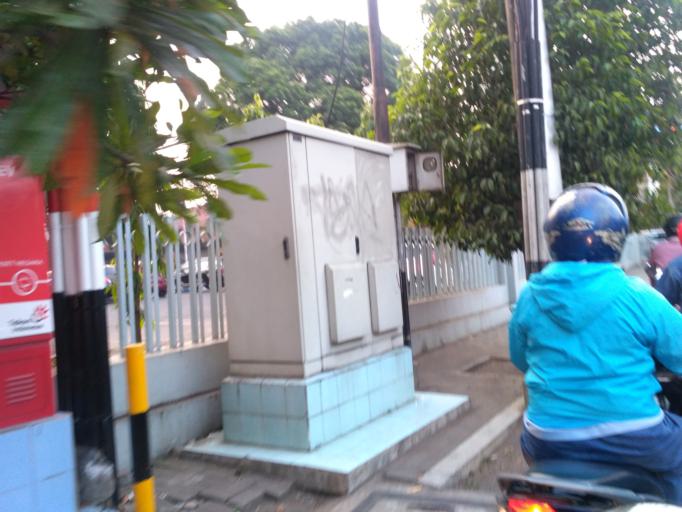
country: ID
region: East Java
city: Malang
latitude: -7.9911
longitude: 112.6342
